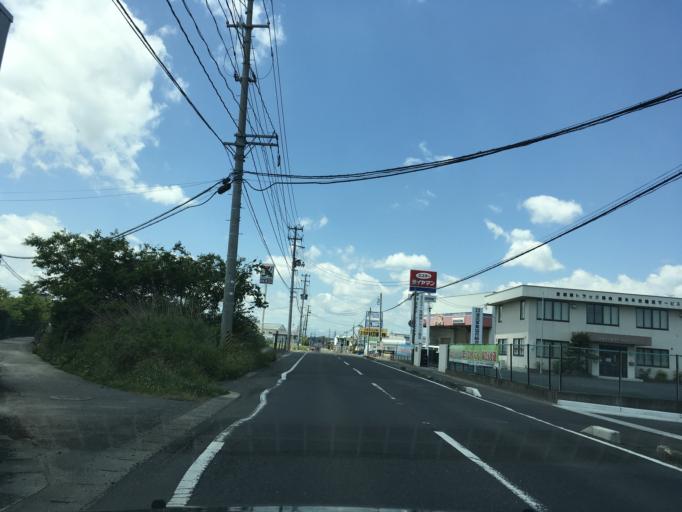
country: JP
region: Miyagi
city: Wakuya
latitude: 38.6801
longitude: 141.2124
